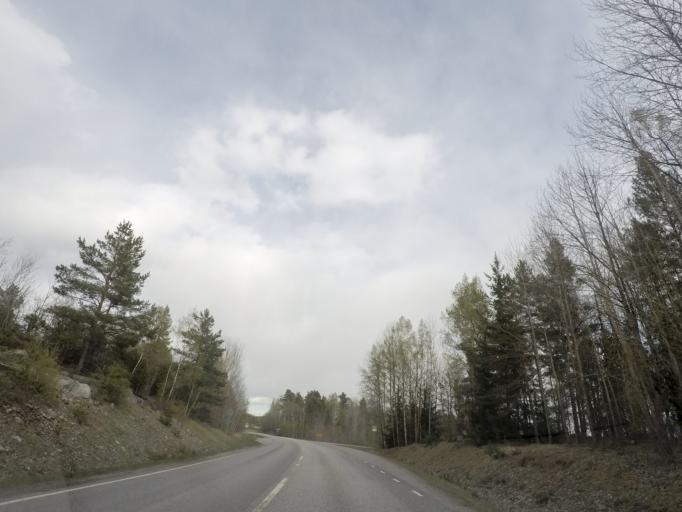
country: SE
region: Vaestmanland
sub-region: Kungsors Kommun
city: Kungsoer
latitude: 59.2849
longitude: 16.1500
